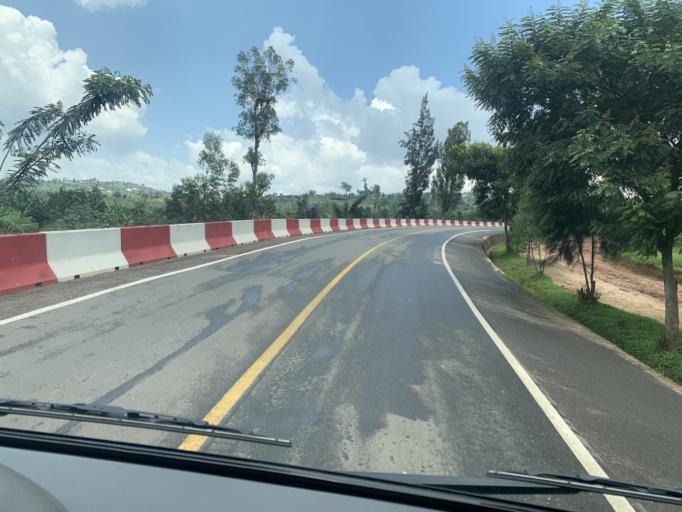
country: RW
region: Southern Province
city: Gitarama
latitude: -2.0076
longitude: 29.8951
